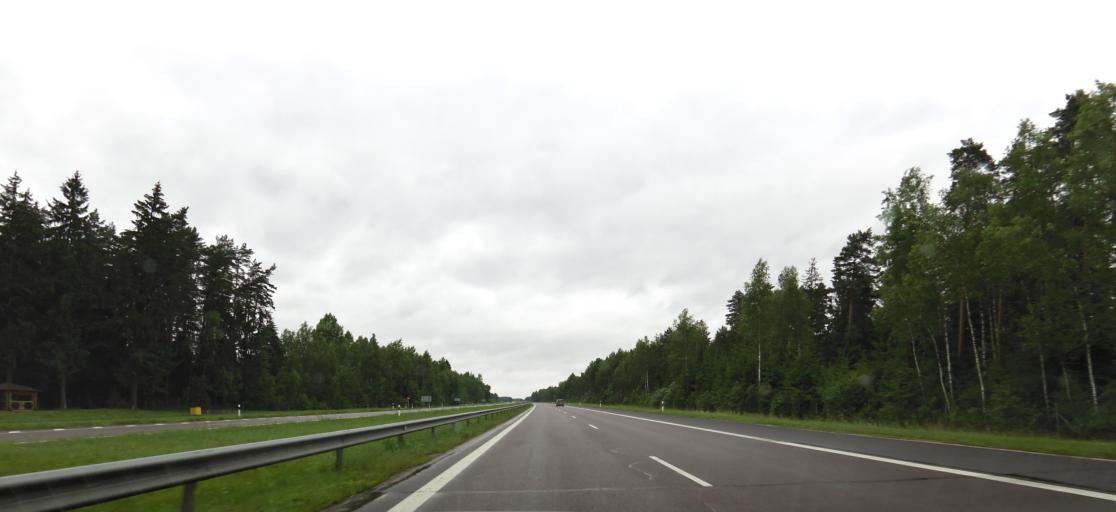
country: LT
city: Sirvintos
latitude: 54.9712
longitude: 24.9476
